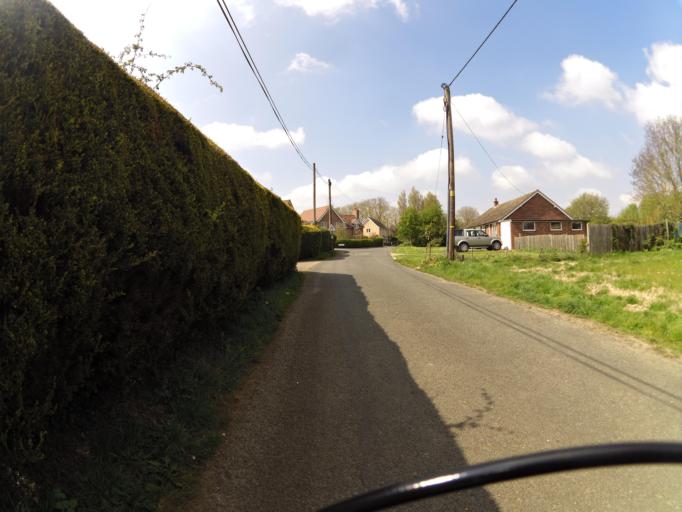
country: GB
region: England
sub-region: Suffolk
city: Hadleigh
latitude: 52.0799
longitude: 0.9892
